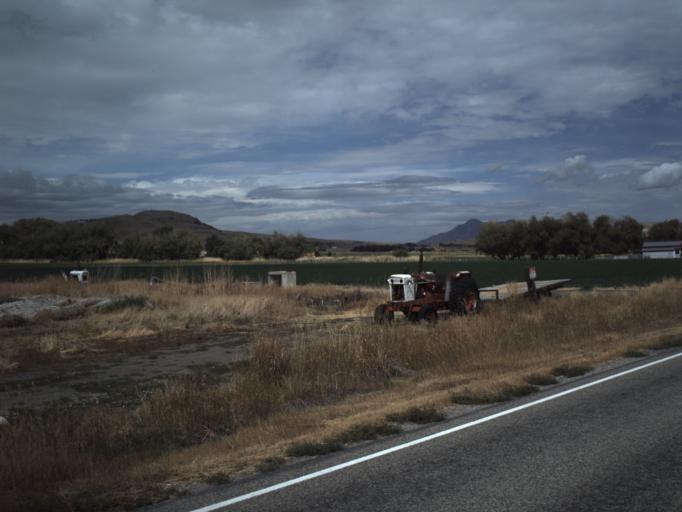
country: US
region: Utah
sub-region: Cache County
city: Mendon
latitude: 41.7268
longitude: -111.9791
